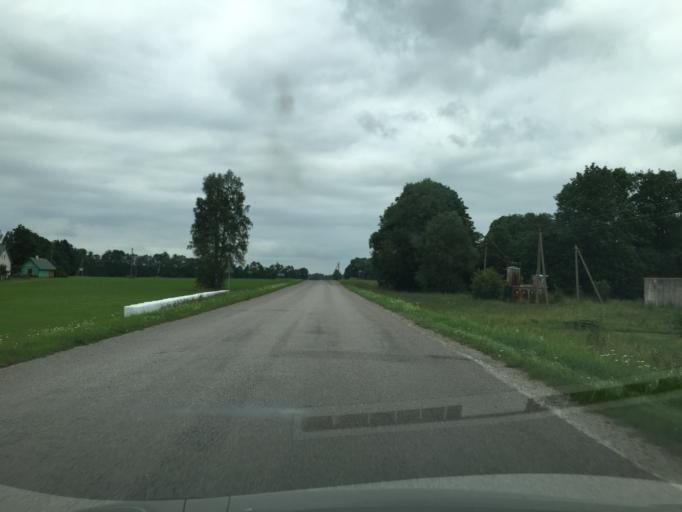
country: EE
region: Raplamaa
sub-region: Jaervakandi vald
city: Jarvakandi
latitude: 58.7959
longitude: 24.9282
